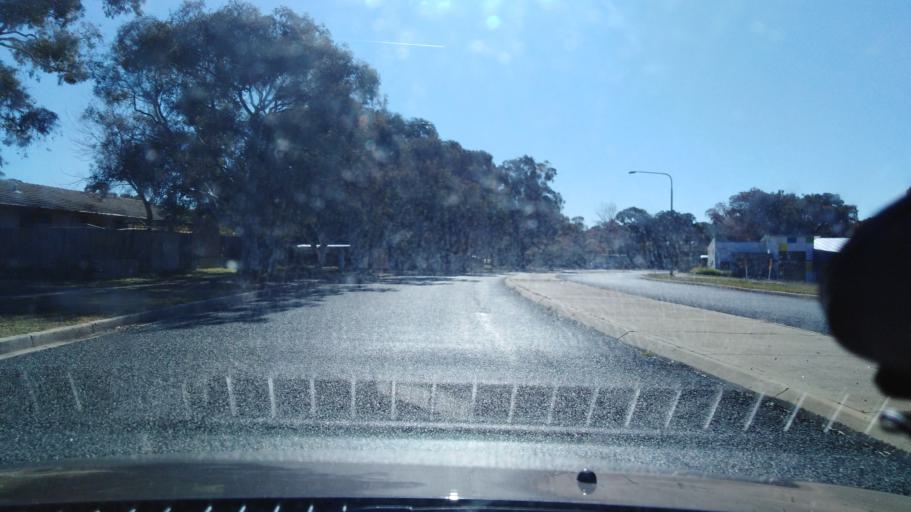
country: AU
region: Australian Capital Territory
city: Forrest
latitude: -35.3483
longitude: 149.0359
